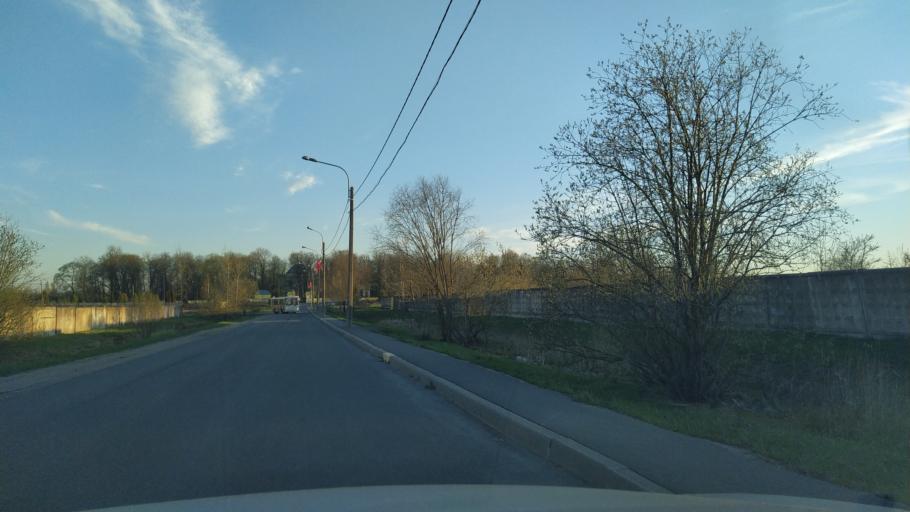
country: RU
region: St.-Petersburg
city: Pushkin
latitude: 59.6968
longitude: 30.3907
